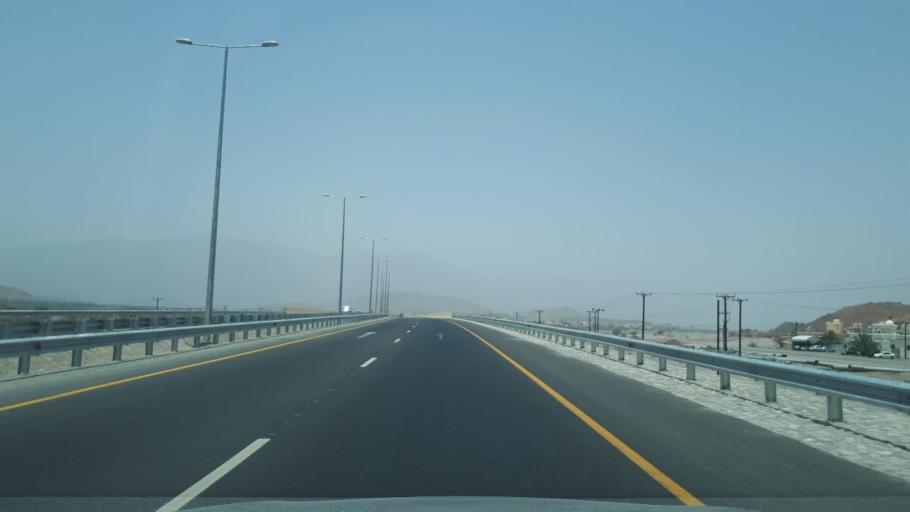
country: OM
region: Al Batinah
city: Rustaq
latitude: 23.4697
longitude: 57.4437
